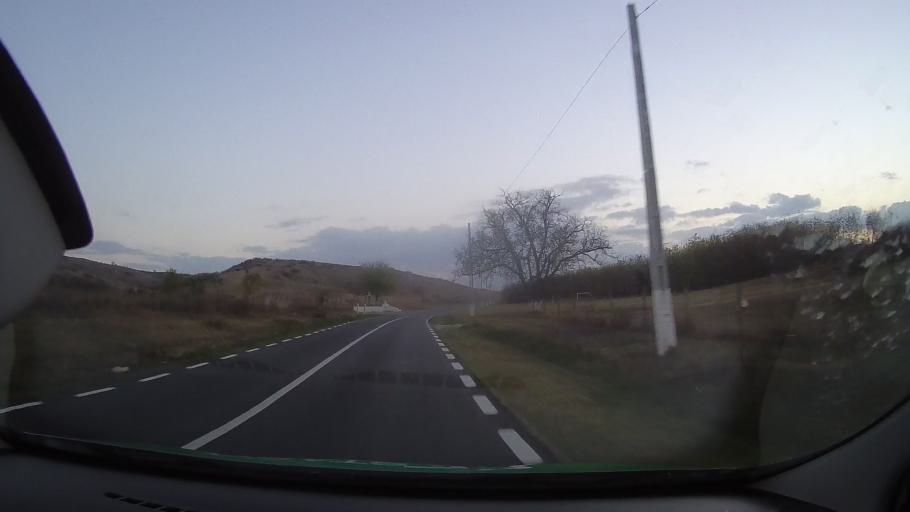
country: RO
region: Constanta
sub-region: Comuna Oltina
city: Oltina
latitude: 44.1521
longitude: 27.6677
